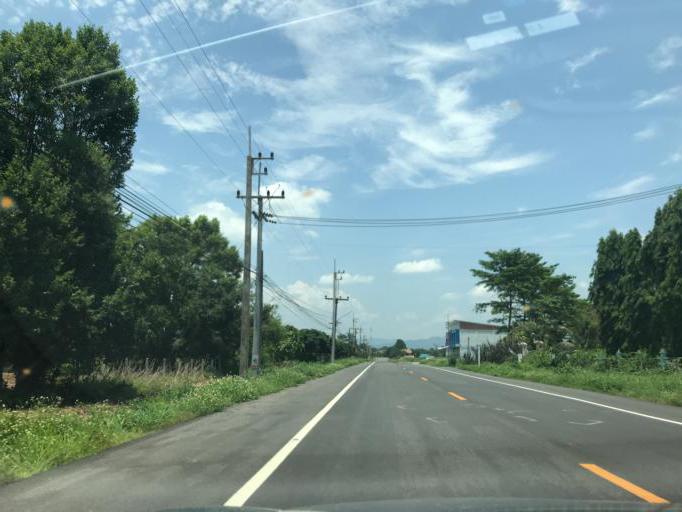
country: TH
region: Phayao
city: Phu Sang
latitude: 19.5896
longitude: 100.3129
